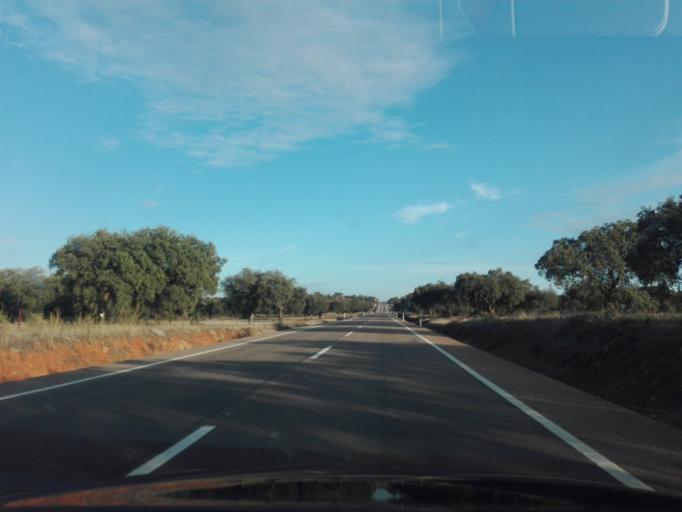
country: ES
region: Extremadura
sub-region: Provincia de Badajoz
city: Usagre
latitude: 38.3688
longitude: -6.2426
